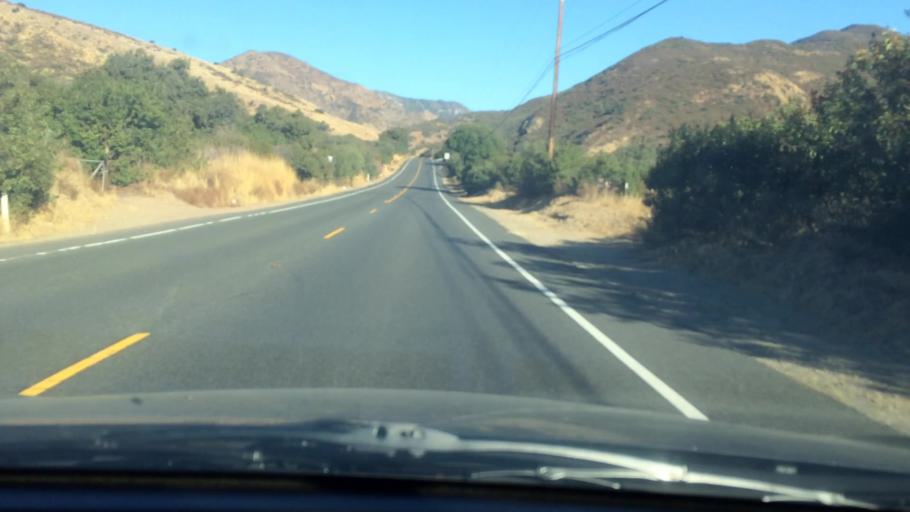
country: US
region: California
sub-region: Orange County
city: Coto De Caza
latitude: 33.5810
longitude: -117.5290
